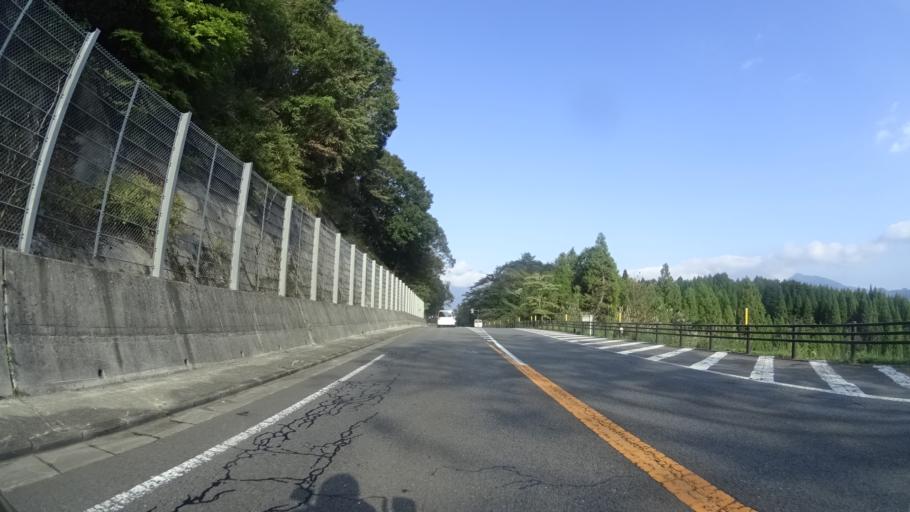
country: JP
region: Oita
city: Tsukawaki
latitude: 33.2528
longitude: 131.3051
